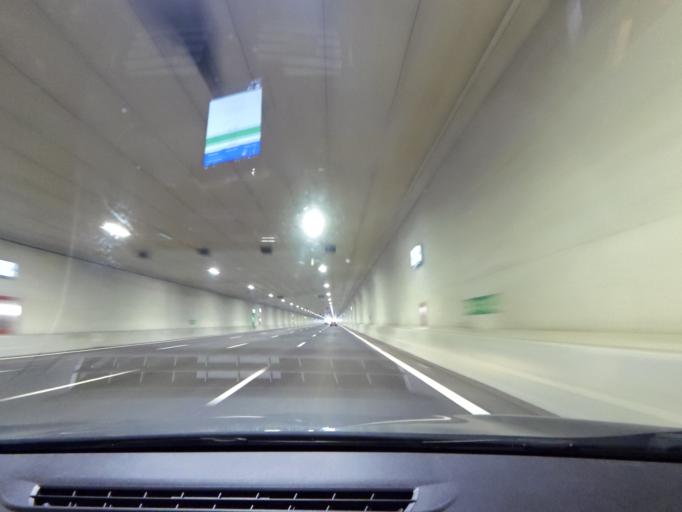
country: NL
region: South Holland
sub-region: Gemeente Vlaardingen
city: Vlaardingen
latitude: 51.9389
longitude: 4.3617
